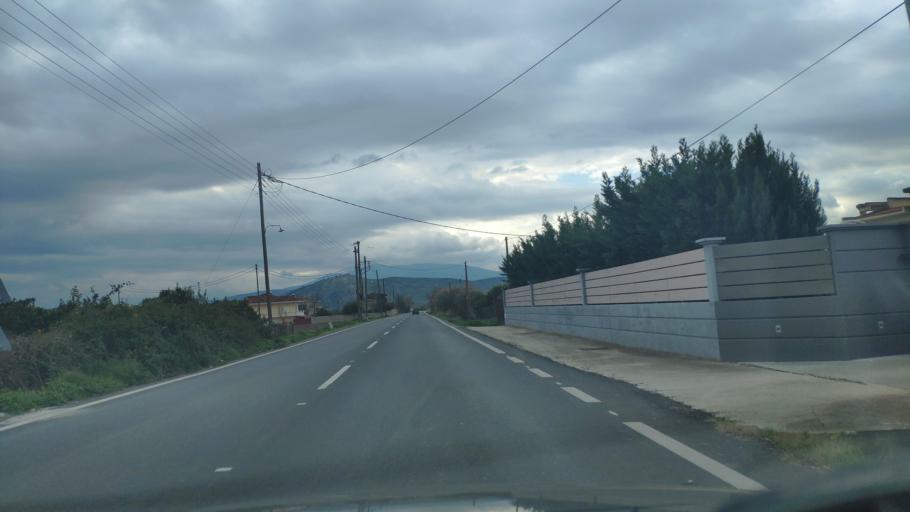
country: GR
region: Peloponnese
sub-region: Nomos Argolidos
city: Nea Kios
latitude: 37.5821
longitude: 22.7096
